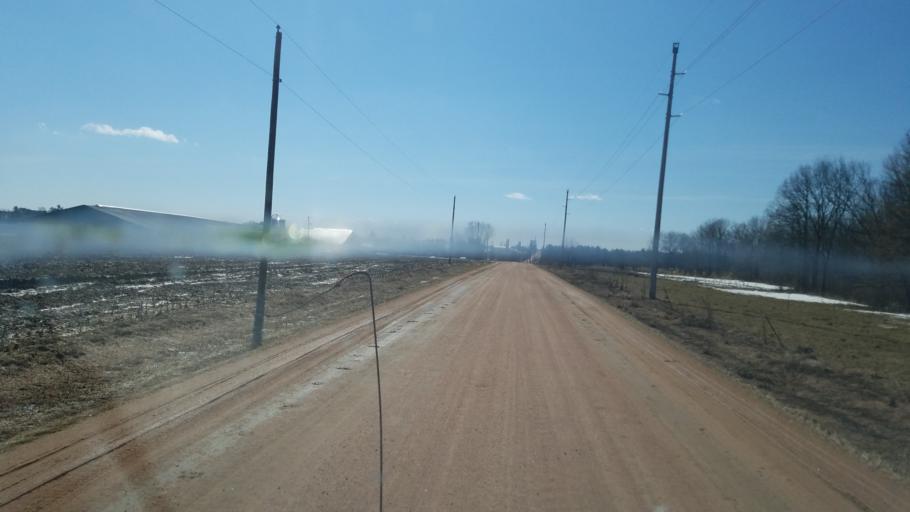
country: US
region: Wisconsin
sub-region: Clark County
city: Loyal
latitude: 44.5960
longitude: -90.3964
